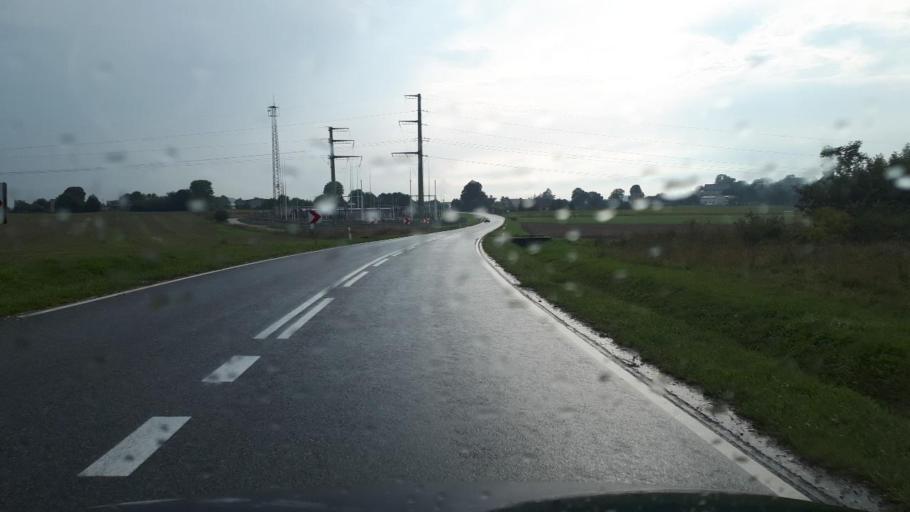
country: PL
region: Silesian Voivodeship
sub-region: Powiat gliwicki
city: Wielowies
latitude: 50.4976
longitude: 18.5958
